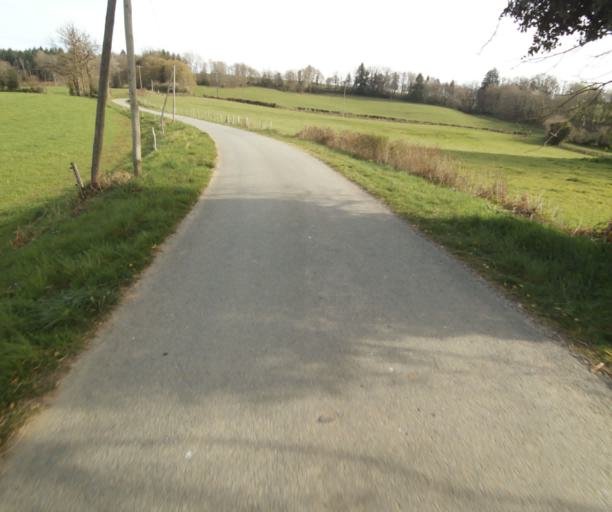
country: FR
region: Limousin
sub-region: Departement de la Correze
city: Chamboulive
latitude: 45.4481
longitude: 1.7505
